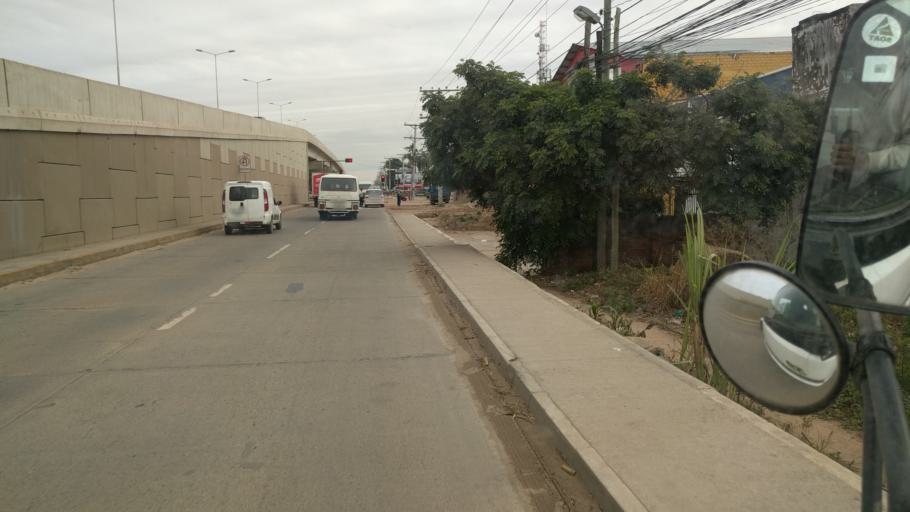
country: BO
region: Santa Cruz
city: Santa Cruz de la Sierra
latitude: -17.7310
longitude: -63.1679
